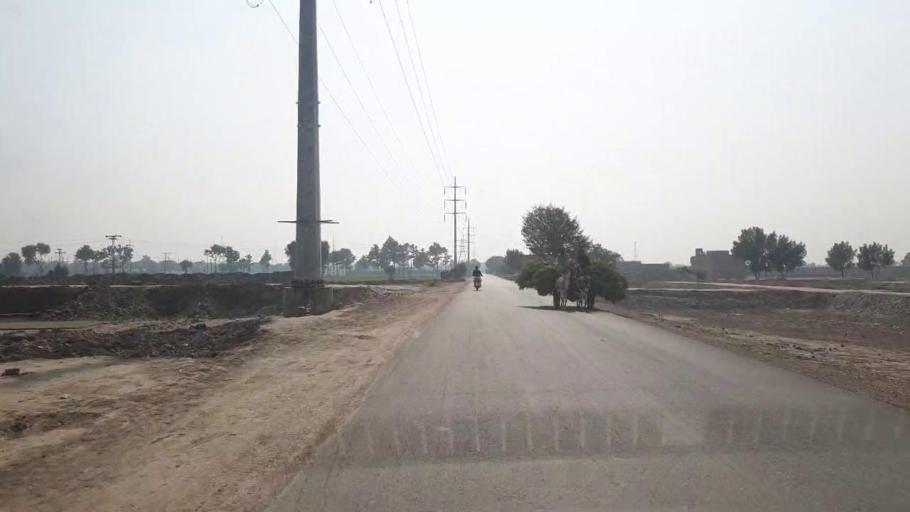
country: PK
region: Sindh
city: Hala
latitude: 25.8288
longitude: 68.4197
